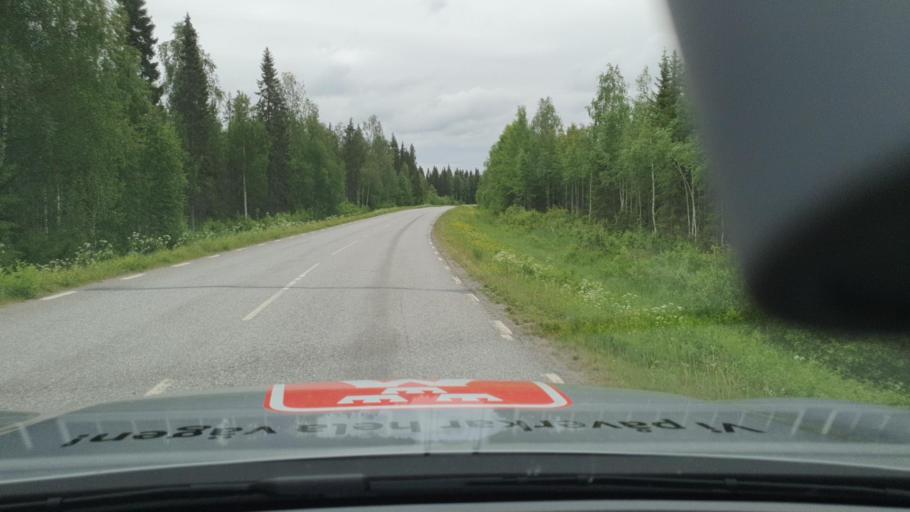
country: SE
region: Norrbotten
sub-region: Lulea Kommun
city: Ranea
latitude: 65.8645
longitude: 22.2326
